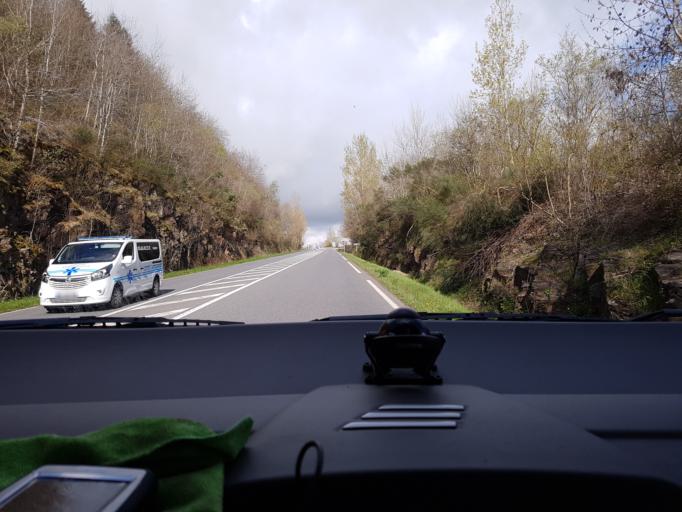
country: FR
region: Midi-Pyrenees
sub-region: Departement de l'Aveyron
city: Moyrazes
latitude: 44.3795
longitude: 2.4326
